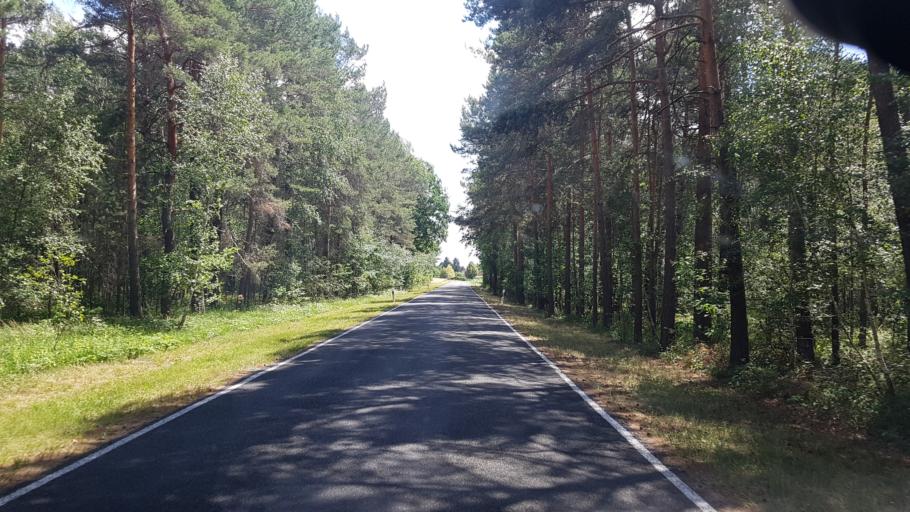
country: DE
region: Brandenburg
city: Schipkau
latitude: 51.5751
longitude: 13.9212
